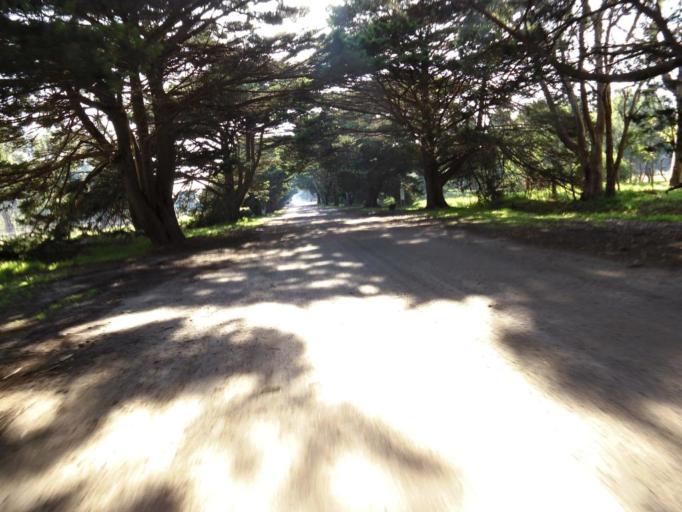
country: AU
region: Victoria
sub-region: Kingston
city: Dingley Village
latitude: -37.9943
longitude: 145.1251
